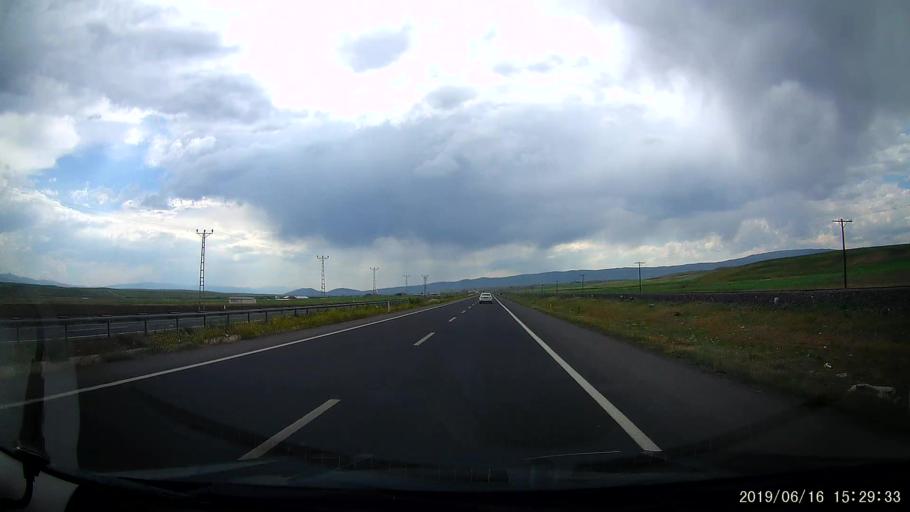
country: TR
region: Erzurum
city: Horasan
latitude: 40.0322
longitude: 42.1291
